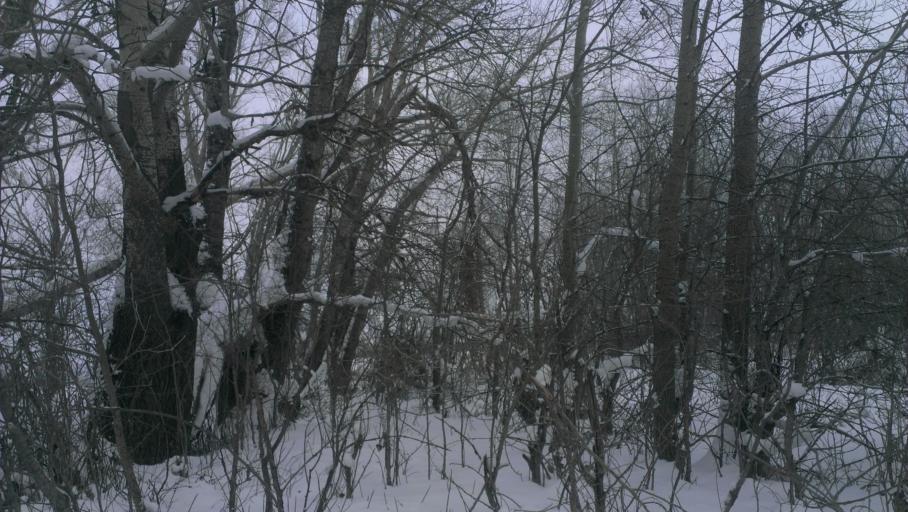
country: RU
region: Altai Krai
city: Zaton
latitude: 53.3161
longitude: 83.8448
